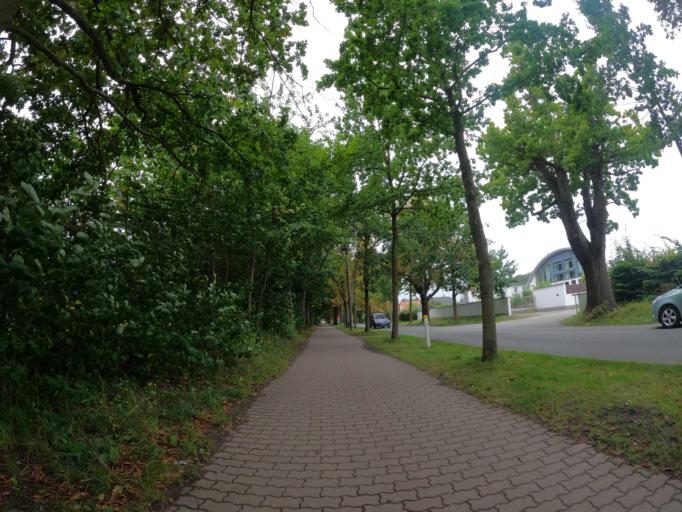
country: DE
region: Mecklenburg-Vorpommern
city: Putbus
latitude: 54.3481
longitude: 13.4898
